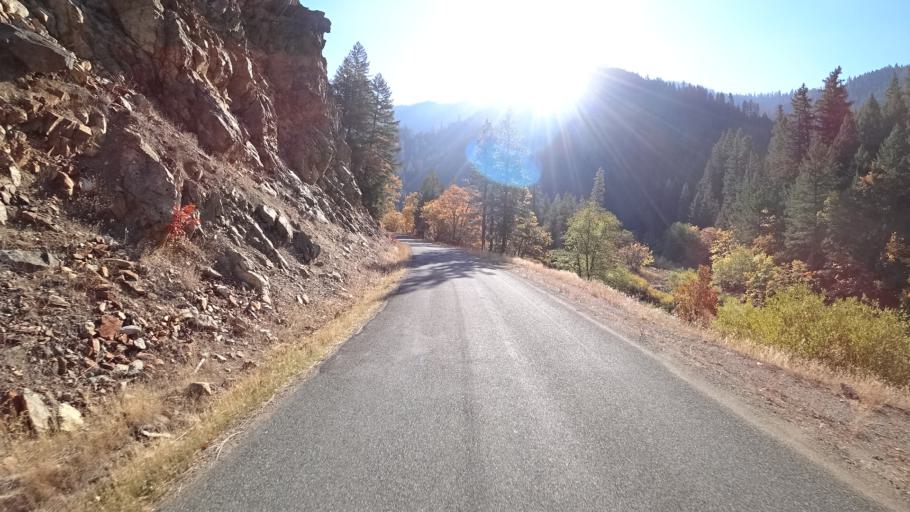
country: US
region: California
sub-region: Siskiyou County
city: Happy Camp
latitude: 41.6340
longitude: -123.0867
